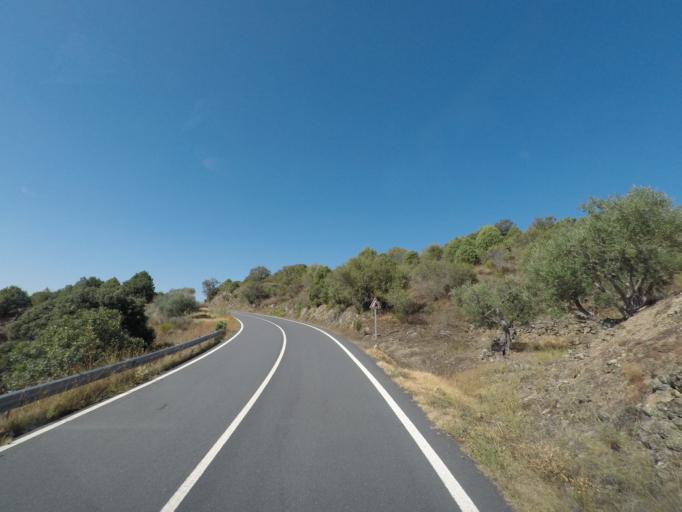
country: ES
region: Castille and Leon
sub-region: Provincia de Salamanca
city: Villarino de los Aires
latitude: 41.2993
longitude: -6.4797
